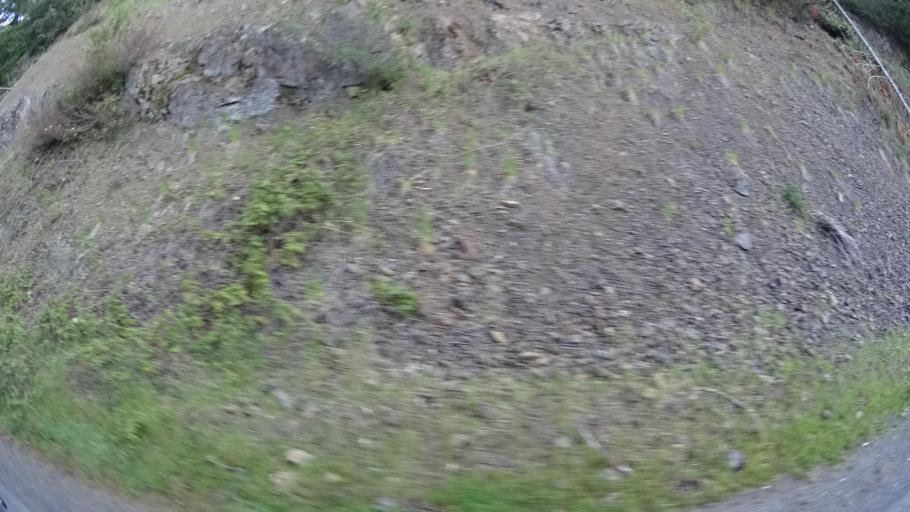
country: US
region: California
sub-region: Humboldt County
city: Hydesville
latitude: 40.6440
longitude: -123.9104
